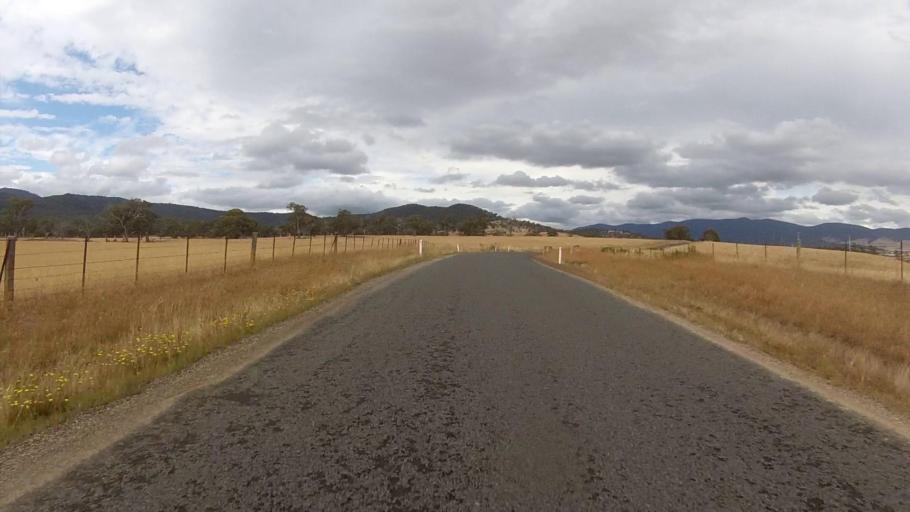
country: AU
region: Tasmania
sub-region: Northern Midlands
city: Evandale
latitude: -41.7917
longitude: 147.7422
